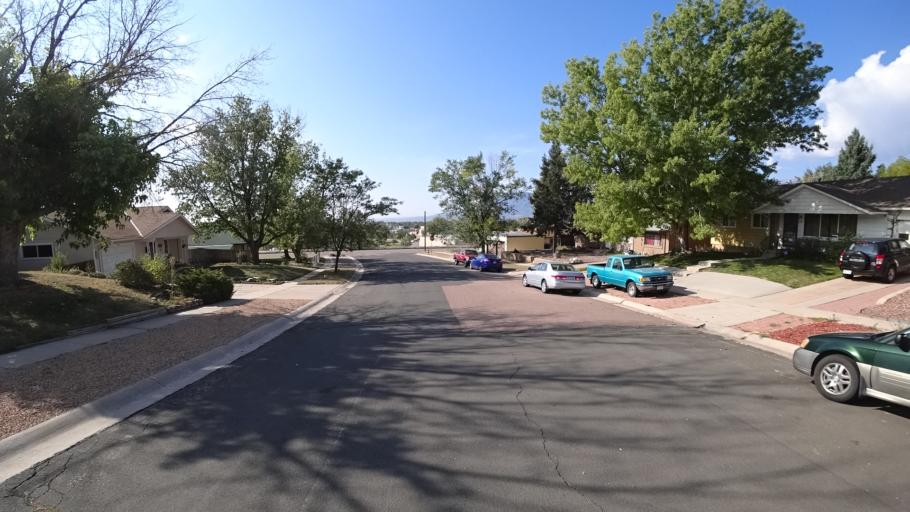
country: US
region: Colorado
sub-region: El Paso County
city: Colorado Springs
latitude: 38.8514
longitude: -104.7735
